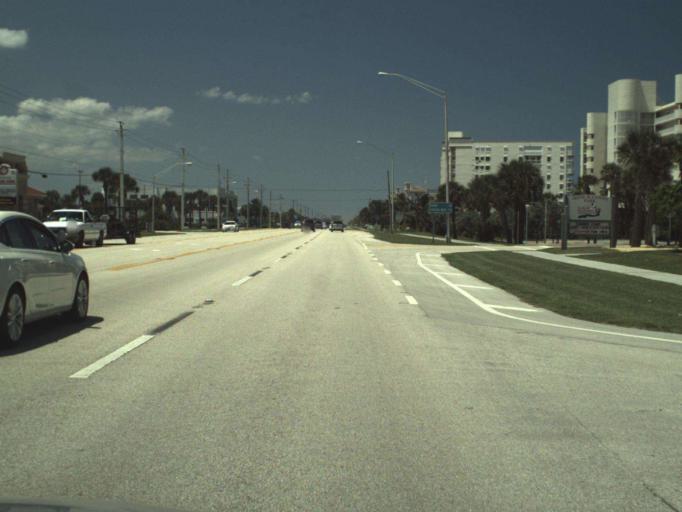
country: US
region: Florida
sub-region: Brevard County
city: Indian Harbour Beach
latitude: 28.1398
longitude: -80.5812
